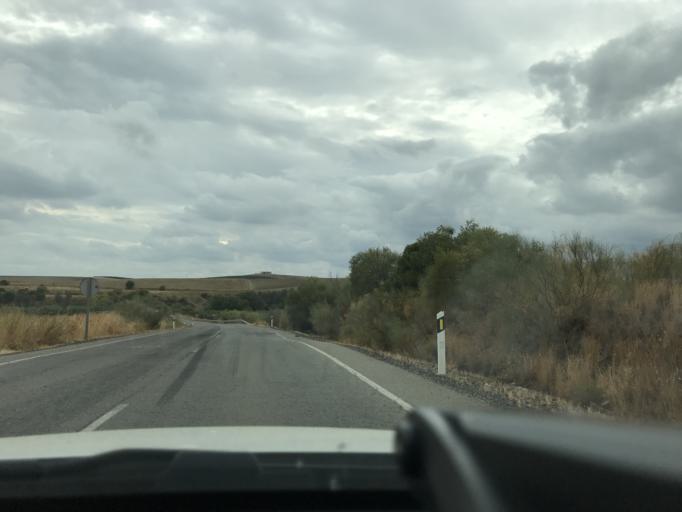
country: ES
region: Andalusia
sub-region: Provincia de Sevilla
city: Cantillana
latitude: 37.6246
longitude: -5.7879
